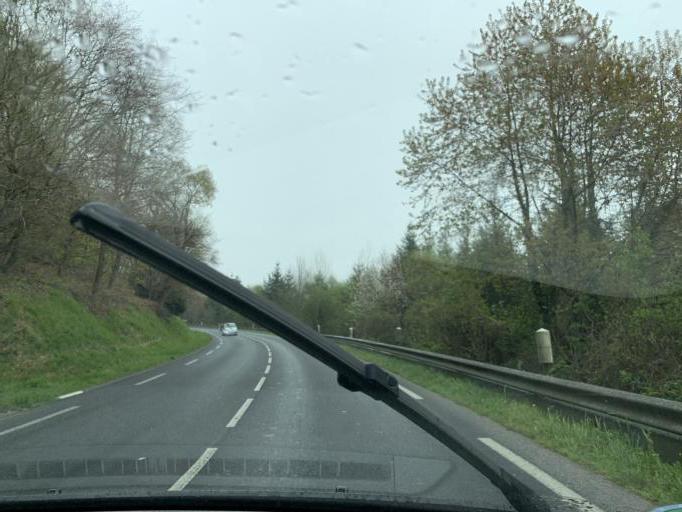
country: FR
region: Haute-Normandie
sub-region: Departement de la Seine-Maritime
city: Cany-Barville
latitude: 49.7834
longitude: 0.6507
